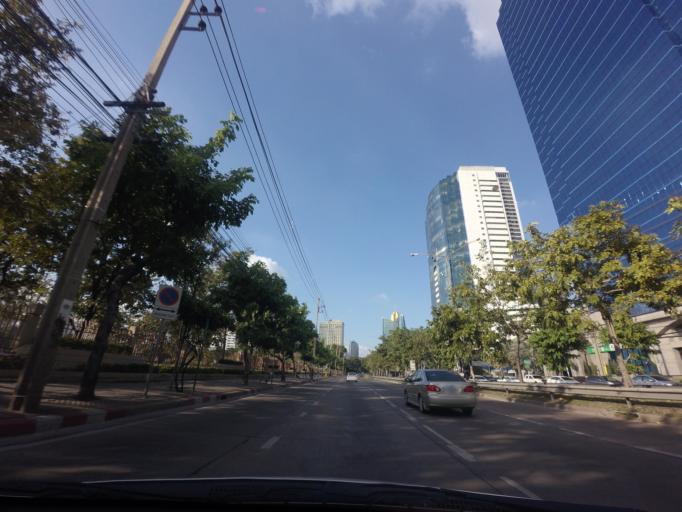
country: TH
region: Bangkok
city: Khlong Toei
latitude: 13.7309
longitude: 100.5593
